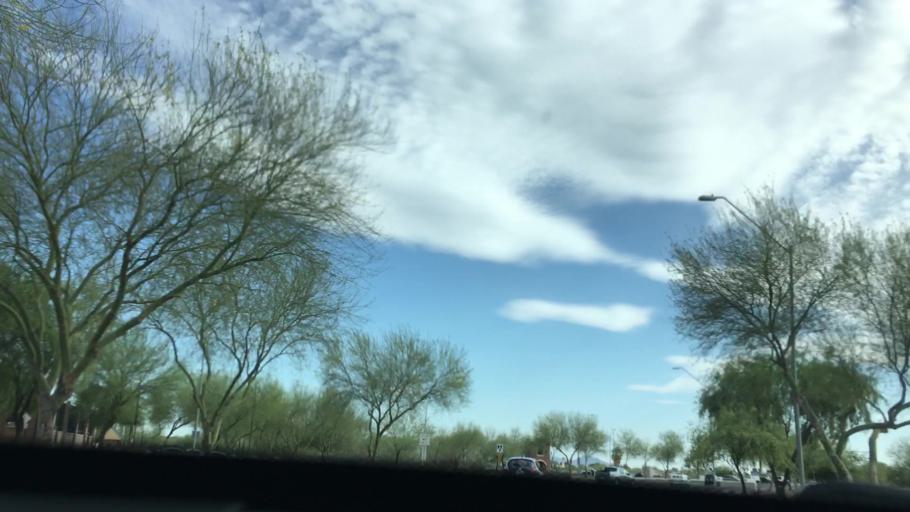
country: US
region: Arizona
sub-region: Maricopa County
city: Peoria
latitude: 33.5798
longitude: -112.2318
